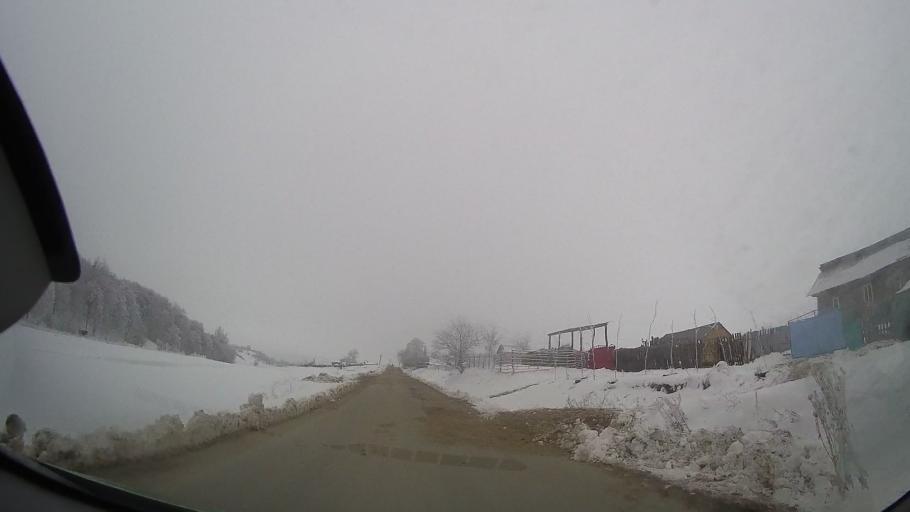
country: RO
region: Neamt
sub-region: Comuna Pancesti
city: Pancesti
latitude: 46.9126
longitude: 27.1600
